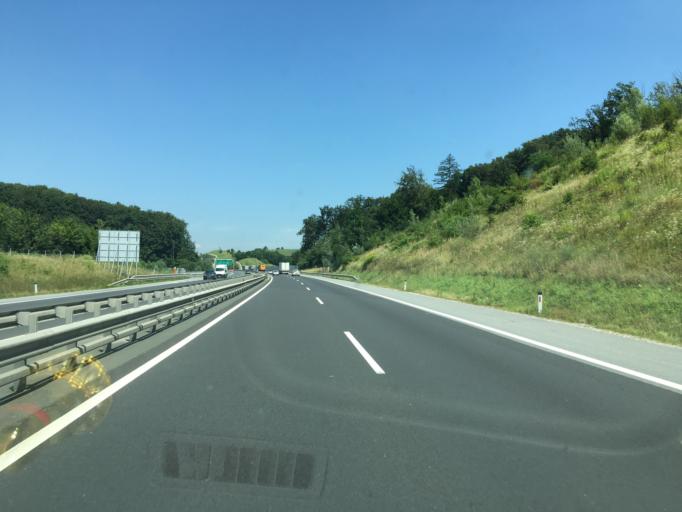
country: SI
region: Pesnica
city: Pesnica pri Mariboru
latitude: 46.5745
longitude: 15.6890
